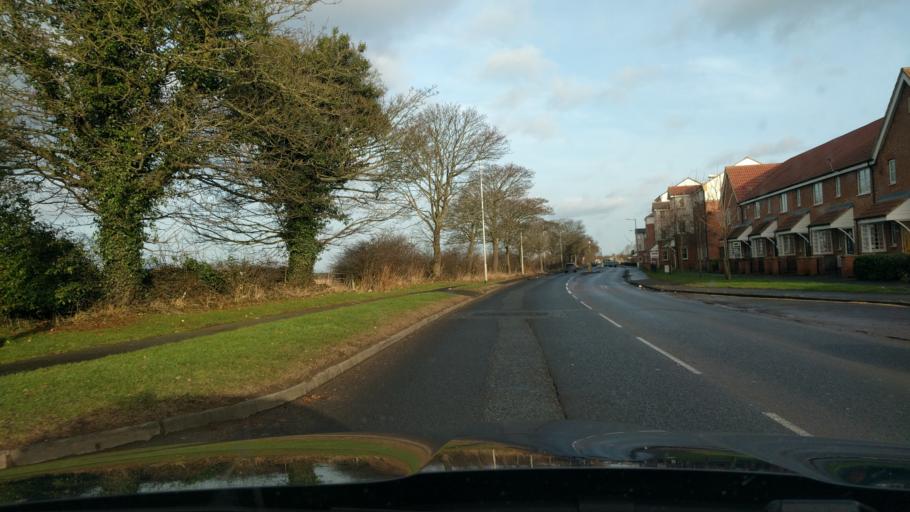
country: GB
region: England
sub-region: Northumberland
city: Ashington
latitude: 55.1869
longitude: -1.5957
